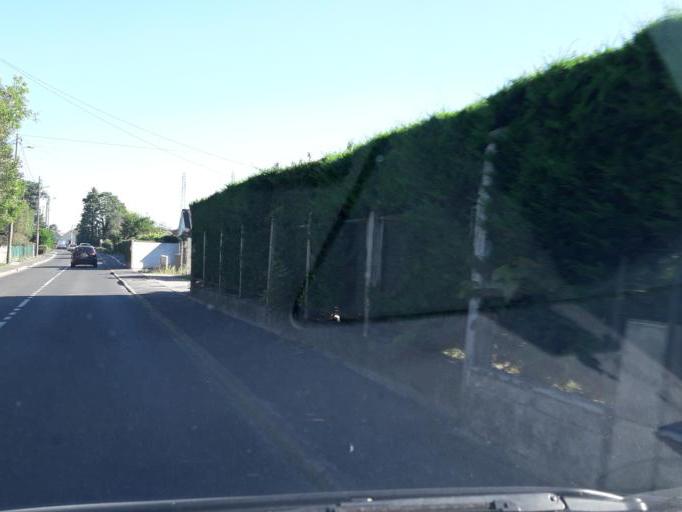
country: FR
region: Ile-de-France
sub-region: Departement de l'Essonne
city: Itteville
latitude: 48.5234
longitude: 2.3492
